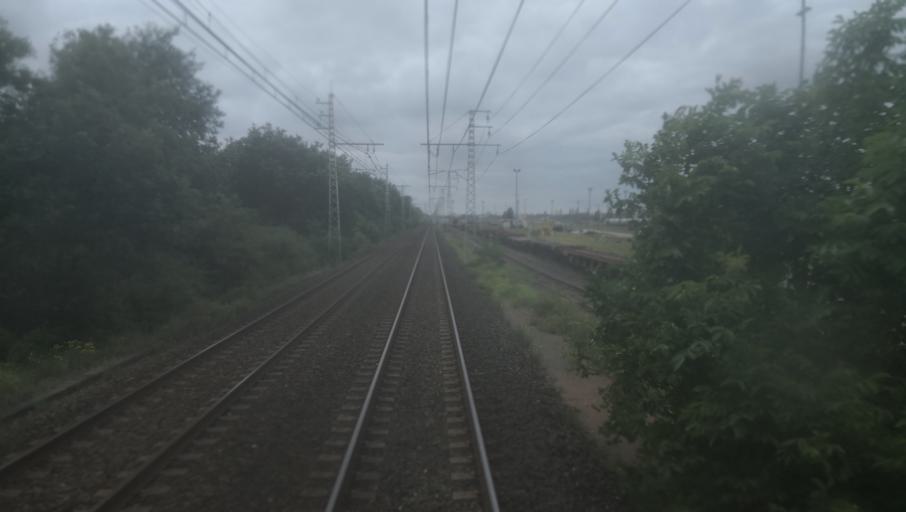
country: FR
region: Midi-Pyrenees
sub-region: Departement de la Haute-Garonne
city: Fenouillet
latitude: 43.6927
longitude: 1.3962
